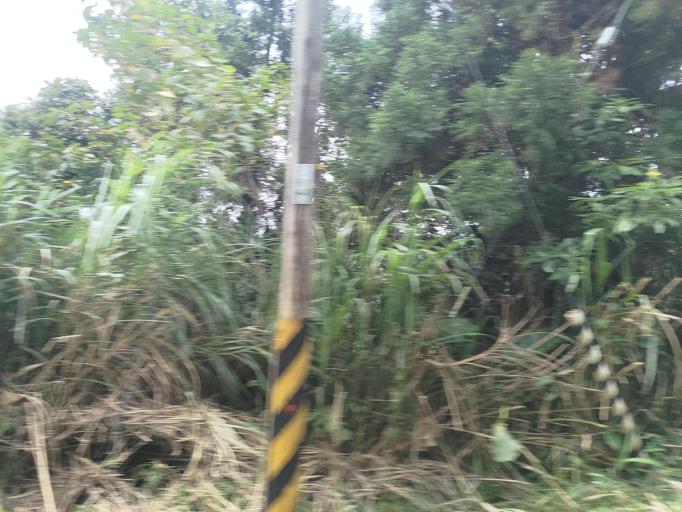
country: TW
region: Taiwan
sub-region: Hsinchu
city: Hsinchu
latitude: 24.6259
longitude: 121.0890
